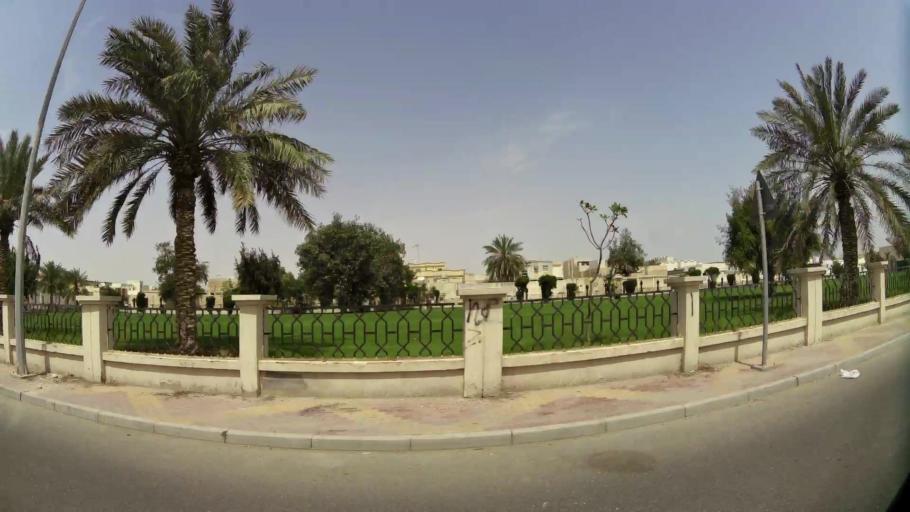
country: QA
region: Baladiyat ad Dawhah
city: Doha
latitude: 25.3147
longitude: 51.4799
